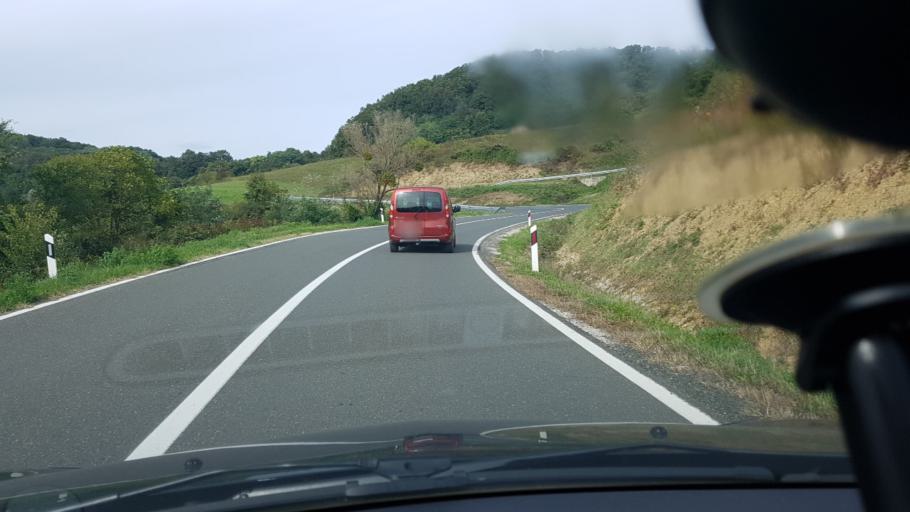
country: HR
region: Varazdinska
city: Ljubescica
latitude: 46.1103
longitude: 16.3555
